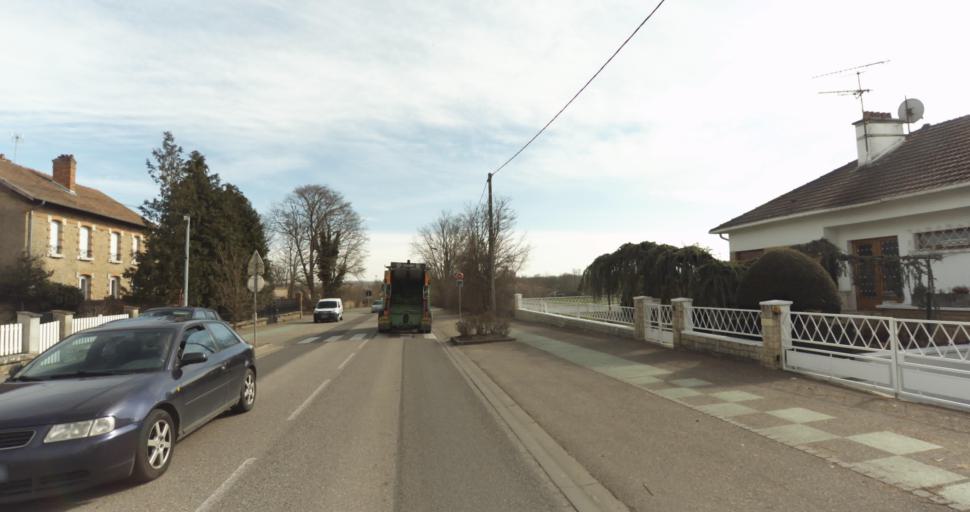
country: FR
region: Lorraine
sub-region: Departement de Meurthe-et-Moselle
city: Jarny
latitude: 49.1527
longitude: 5.8985
